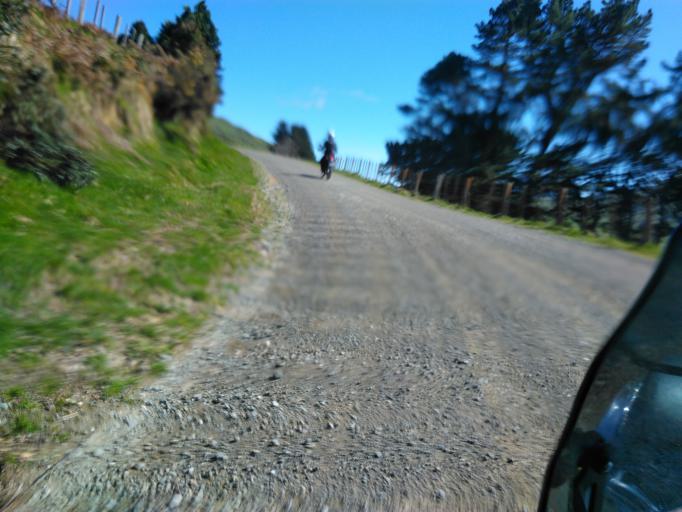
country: NZ
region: Bay of Plenty
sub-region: Opotiki District
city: Opotiki
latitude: -38.3552
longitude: 177.5897
